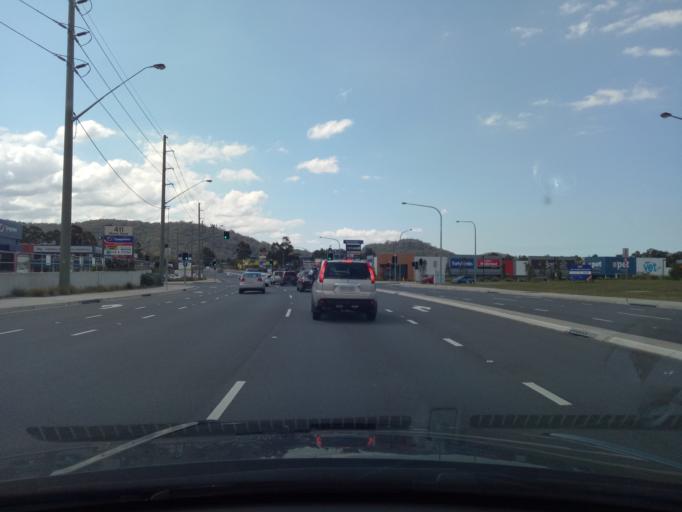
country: AU
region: New South Wales
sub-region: Gosford Shire
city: Point Clare
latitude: -33.4255
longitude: 151.3189
